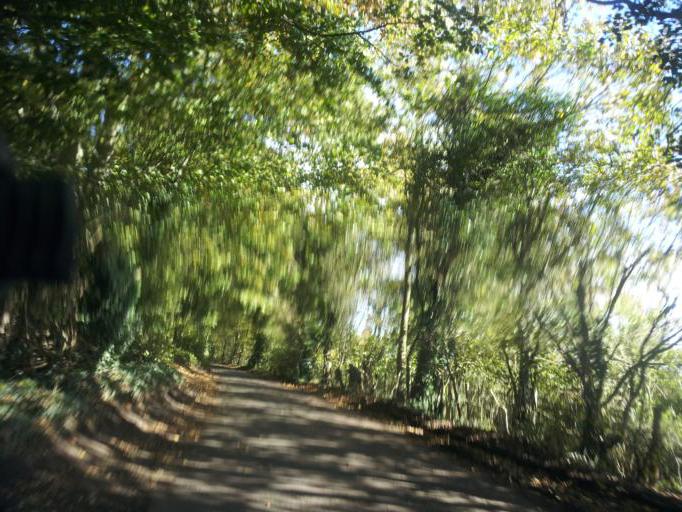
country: GB
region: England
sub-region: Kent
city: Rainham
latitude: 51.3370
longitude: 0.6252
